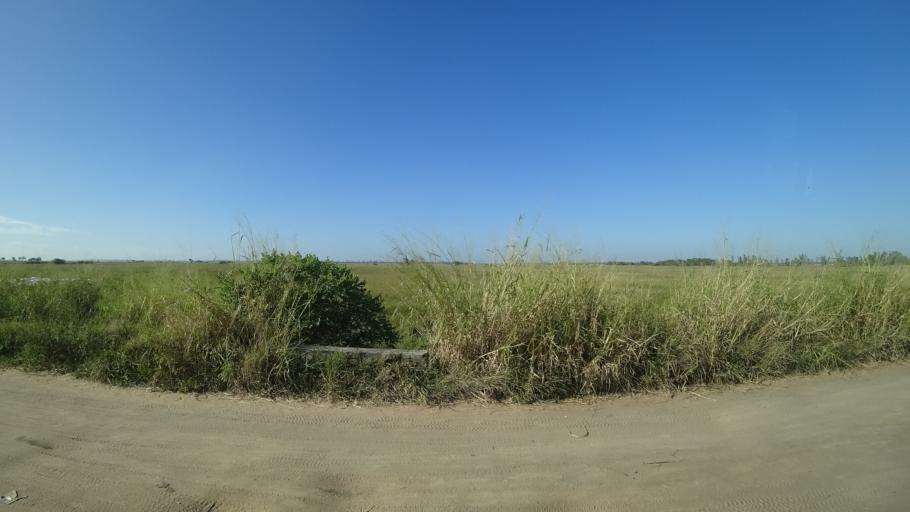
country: MZ
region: Sofala
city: Beira
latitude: -19.7631
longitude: 34.9045
